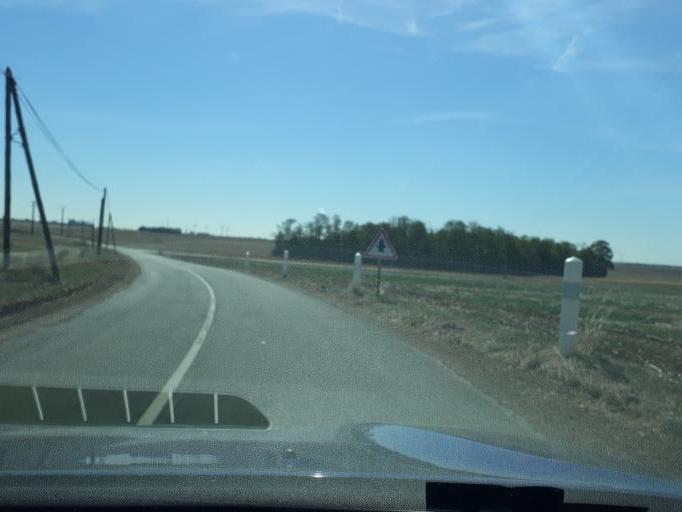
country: FR
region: Centre
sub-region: Departement du Loir-et-Cher
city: Ouzouer-le-Marche
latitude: 47.9353
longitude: 1.5161
